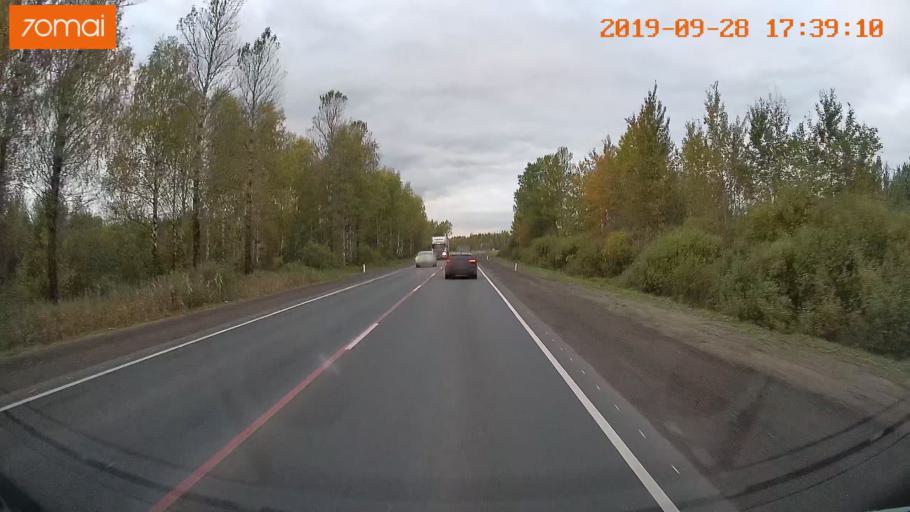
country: RU
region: Jaroslavl
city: Yaroslavl
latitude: 57.5440
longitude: 39.9267
